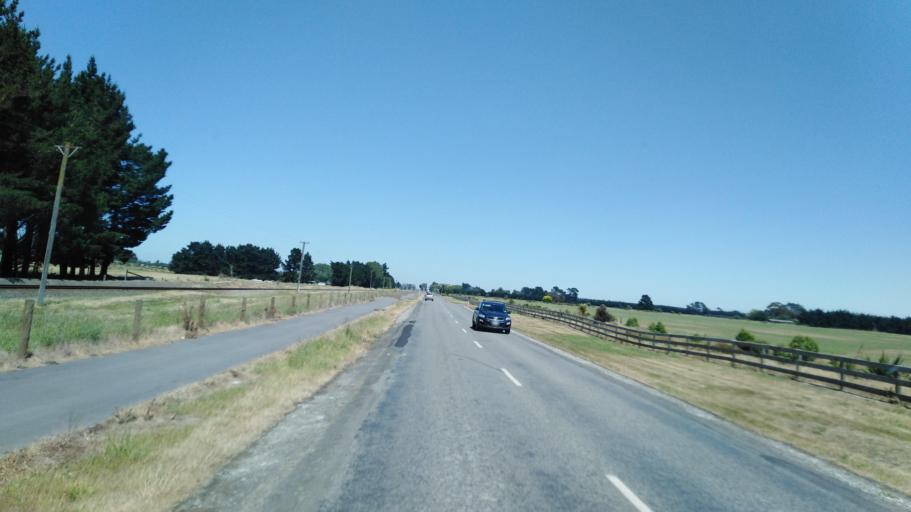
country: NZ
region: Canterbury
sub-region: Selwyn District
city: Prebbleton
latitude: -43.5618
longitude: 172.4539
